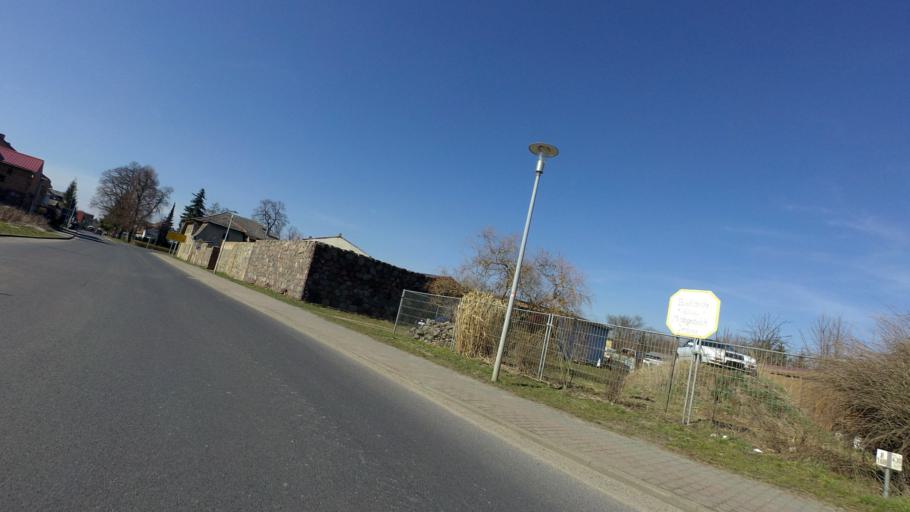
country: DE
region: Brandenburg
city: Werftpfuhl
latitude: 52.7368
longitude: 13.8394
